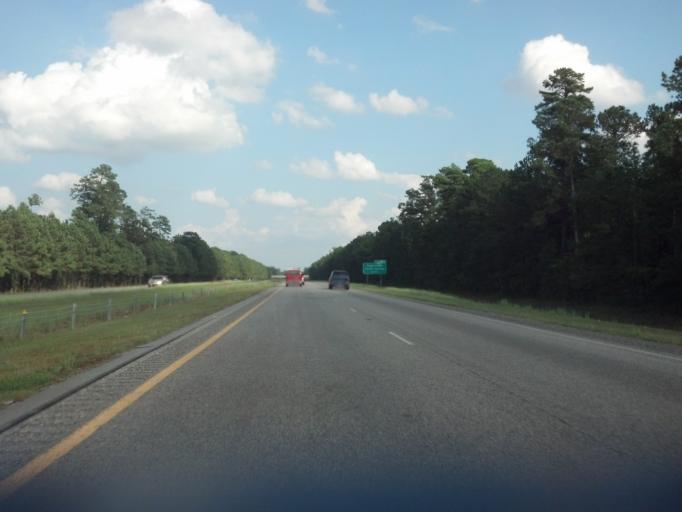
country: US
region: North Carolina
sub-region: Edgecombe County
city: Tarboro
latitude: 35.8956
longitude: -77.6299
